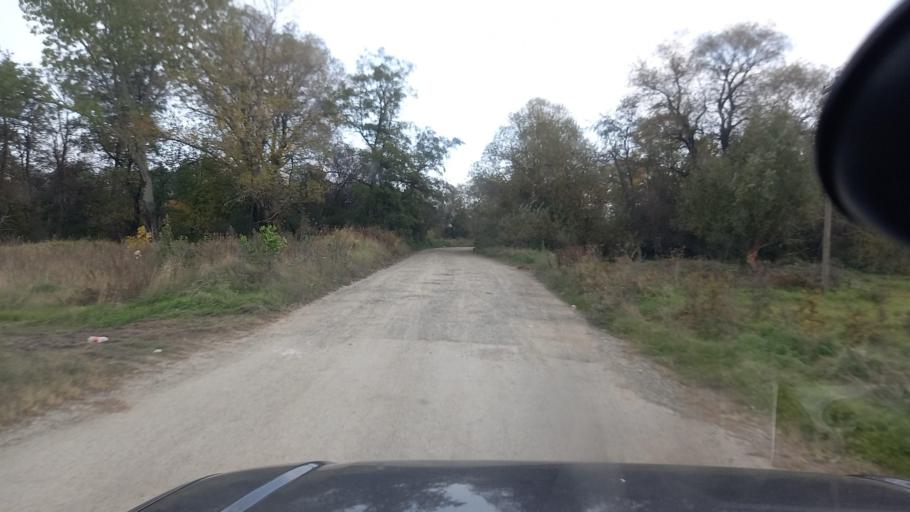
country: RU
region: Krasnodarskiy
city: Shedok
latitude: 44.1840
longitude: 40.8426
